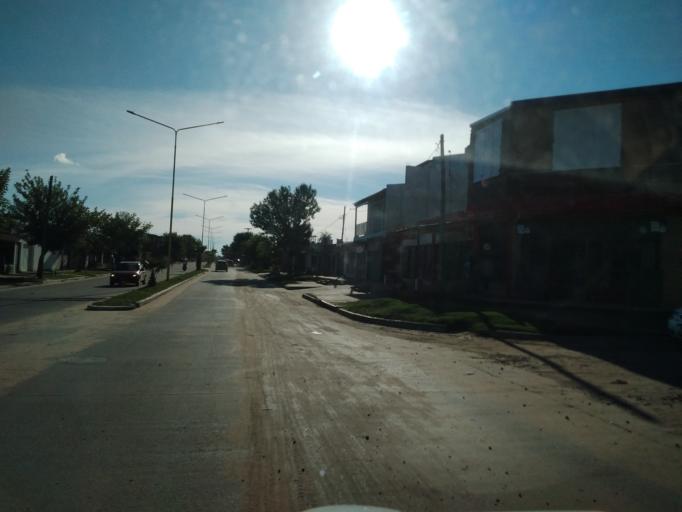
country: AR
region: Corrientes
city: Corrientes
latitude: -27.5057
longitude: -58.7840
